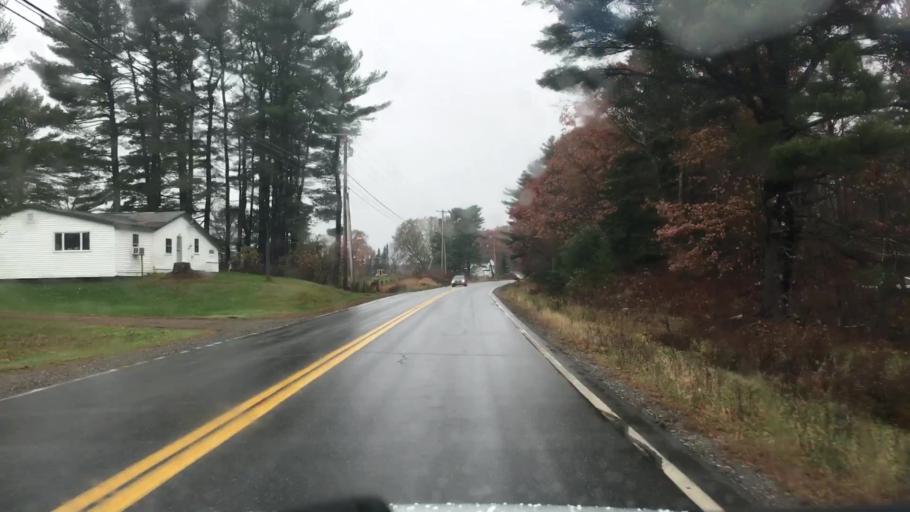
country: US
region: Maine
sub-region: Lincoln County
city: Waldoboro
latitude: 44.1269
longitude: -69.4133
